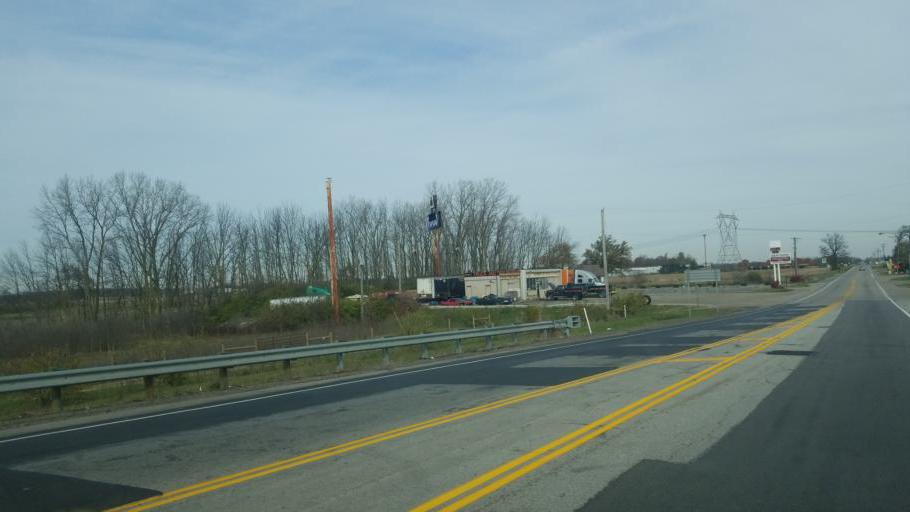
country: US
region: Ohio
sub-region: Madison County
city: London
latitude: 39.9580
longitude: -83.3725
